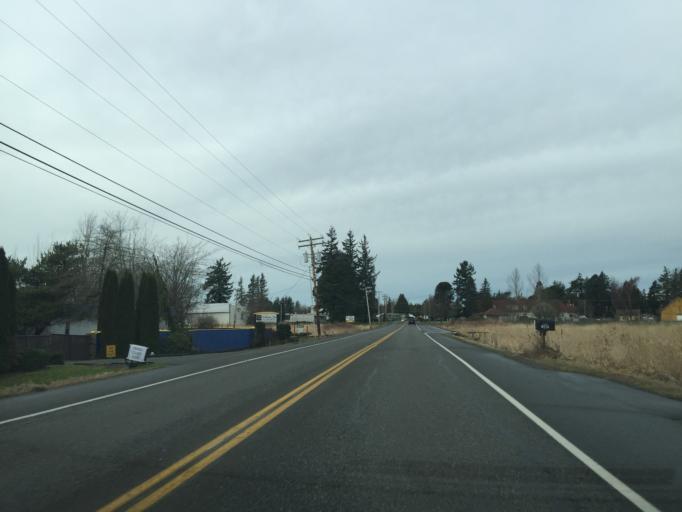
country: US
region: Washington
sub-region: Whatcom County
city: Marietta-Alderwood
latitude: 48.8301
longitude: -122.5384
